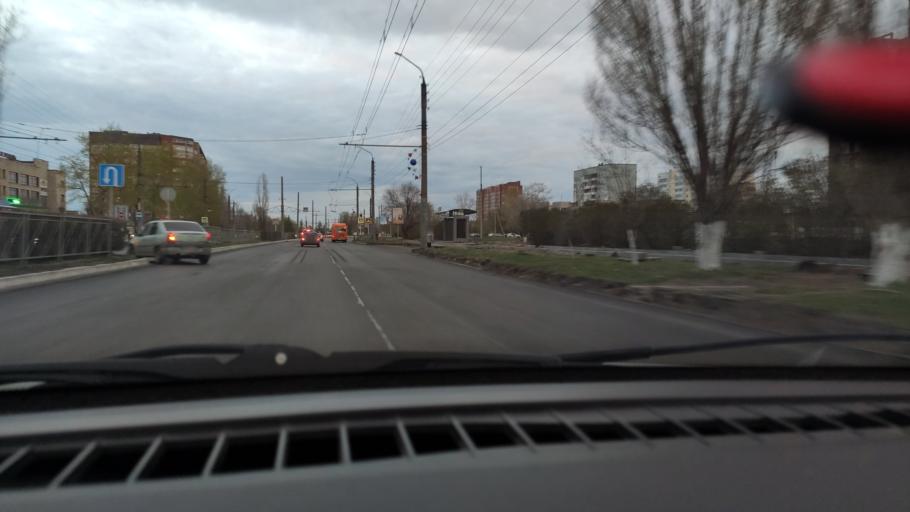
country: RU
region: Orenburg
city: Orenburg
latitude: 51.8149
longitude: 55.1075
